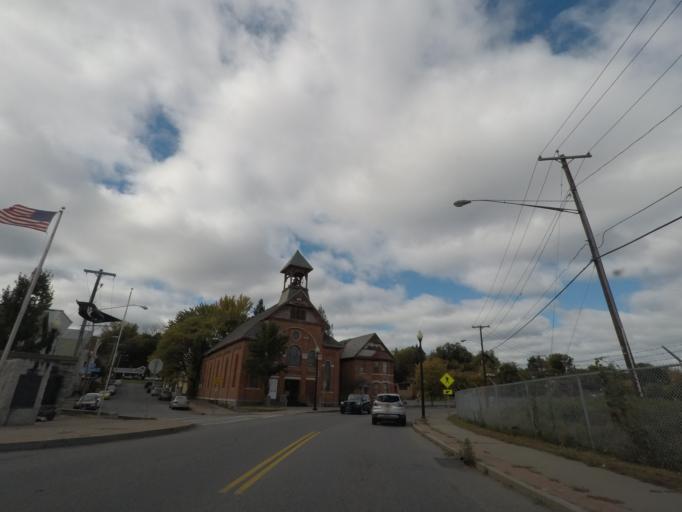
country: US
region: New York
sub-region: Albany County
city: Cohoes
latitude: 42.7839
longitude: -73.7094
